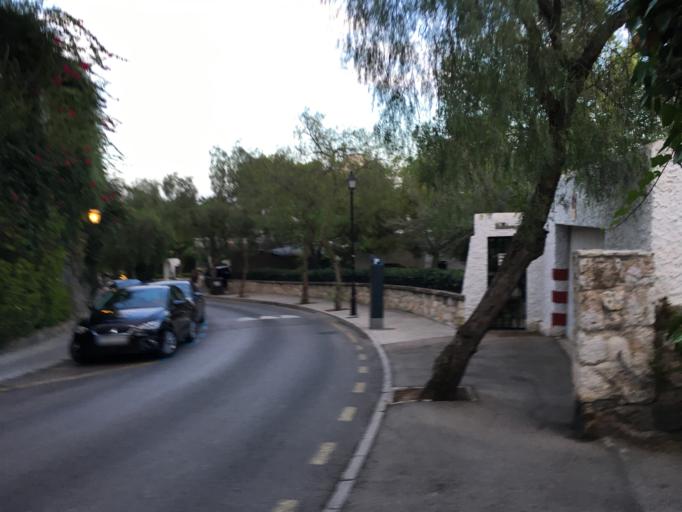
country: ES
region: Balearic Islands
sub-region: Illes Balears
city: Magaluf
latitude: 39.5403
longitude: 2.5927
